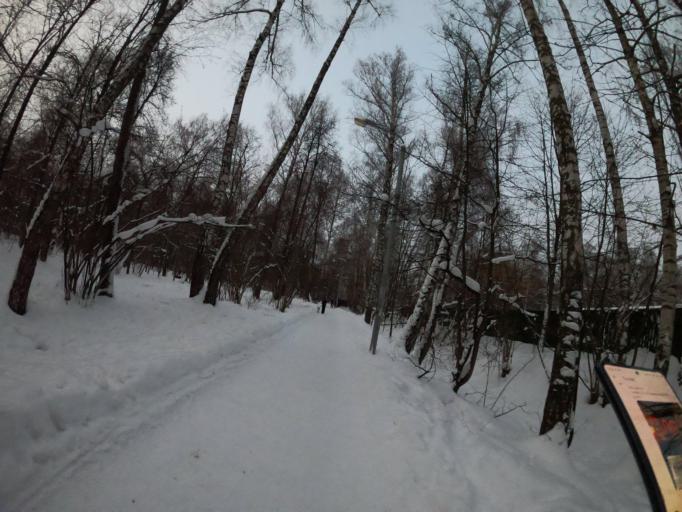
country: RU
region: Moskovskaya
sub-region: Podol'skiy Rayon
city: Podol'sk
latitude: 55.4164
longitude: 37.5259
